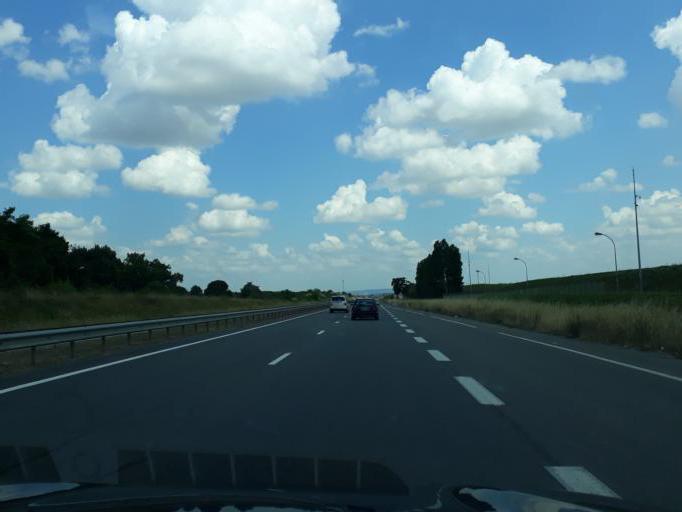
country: FR
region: Centre
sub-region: Departement du Cher
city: Bourges
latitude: 47.0702
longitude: 2.4355
